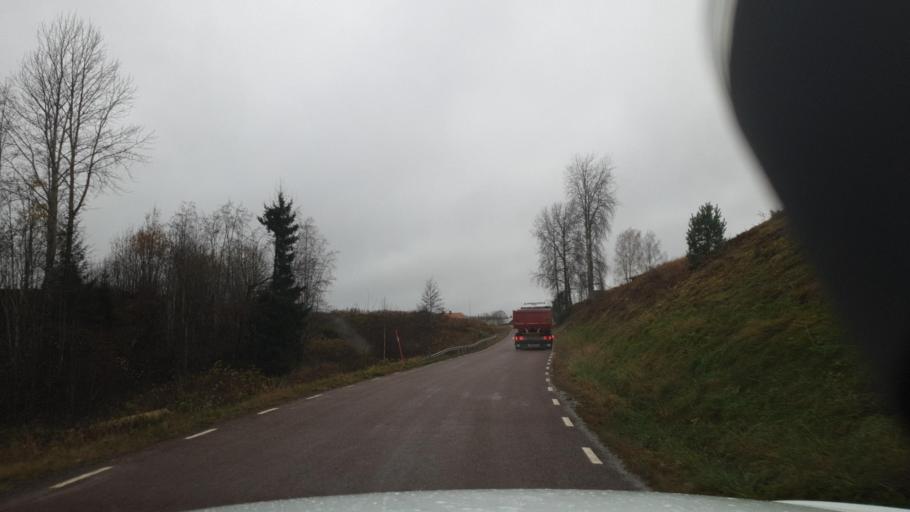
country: SE
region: Vaermland
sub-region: Sunne Kommun
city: Sunne
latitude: 59.7408
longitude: 13.0635
